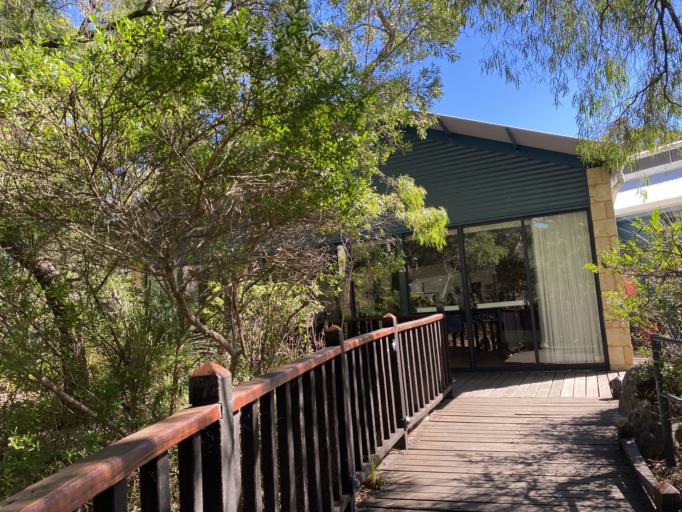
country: AU
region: Western Australia
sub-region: Augusta-Margaret River Shire
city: Margaret River
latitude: -34.0791
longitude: 115.0296
